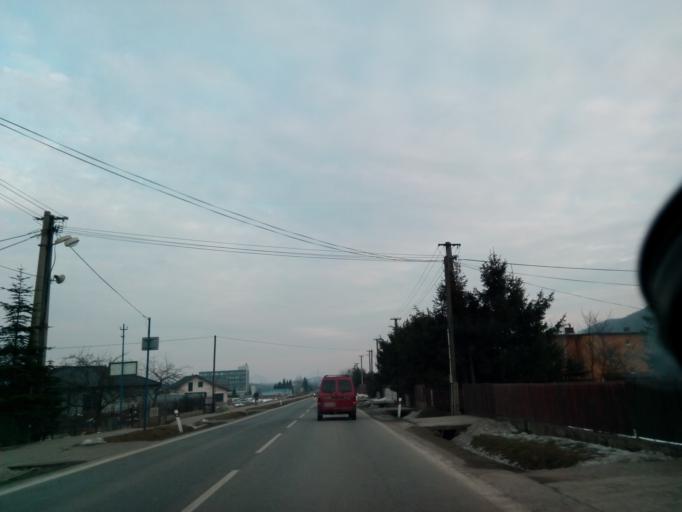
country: SK
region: Presovsky
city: Sabinov
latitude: 49.1208
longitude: 21.0525
